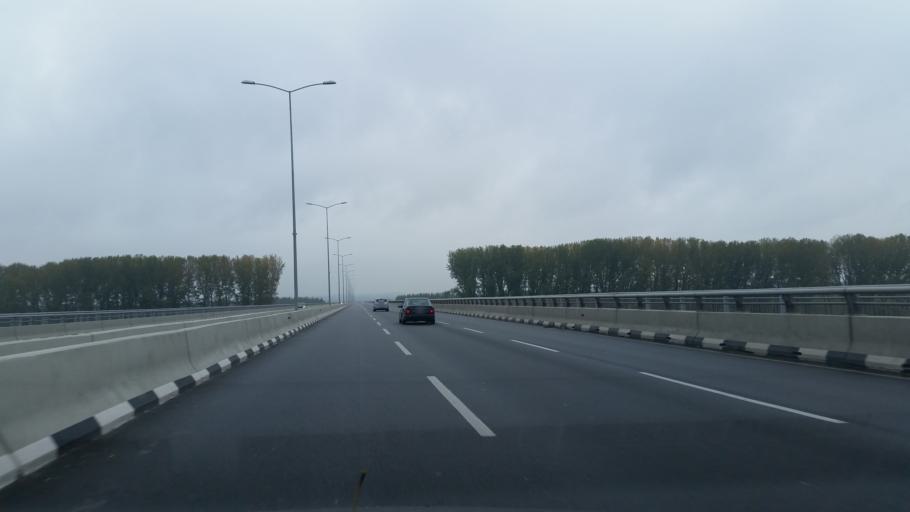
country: RS
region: Central Serbia
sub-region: Belgrade
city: Zemun
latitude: 44.8650
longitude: 20.3815
